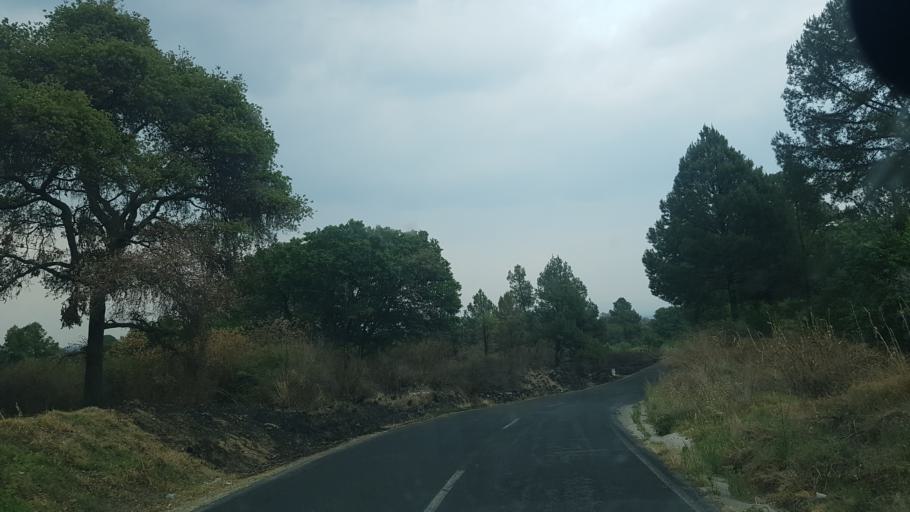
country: MX
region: Puebla
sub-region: Chiautzingo
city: San Nicolas Zecalacoayan
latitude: 19.1898
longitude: -98.4753
